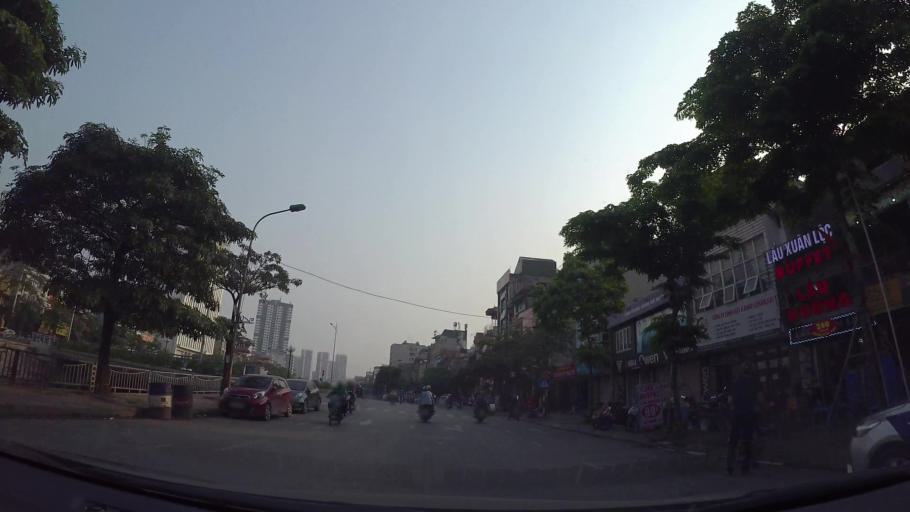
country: VN
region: Ha Noi
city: Thanh Xuan
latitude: 20.9960
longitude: 105.8151
